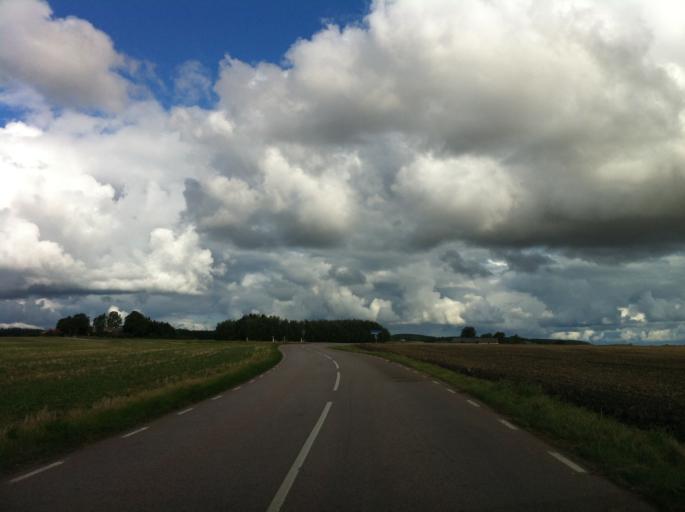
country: SE
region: Skane
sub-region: Eslovs Kommun
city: Eslov
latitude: 55.8769
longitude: 13.2508
